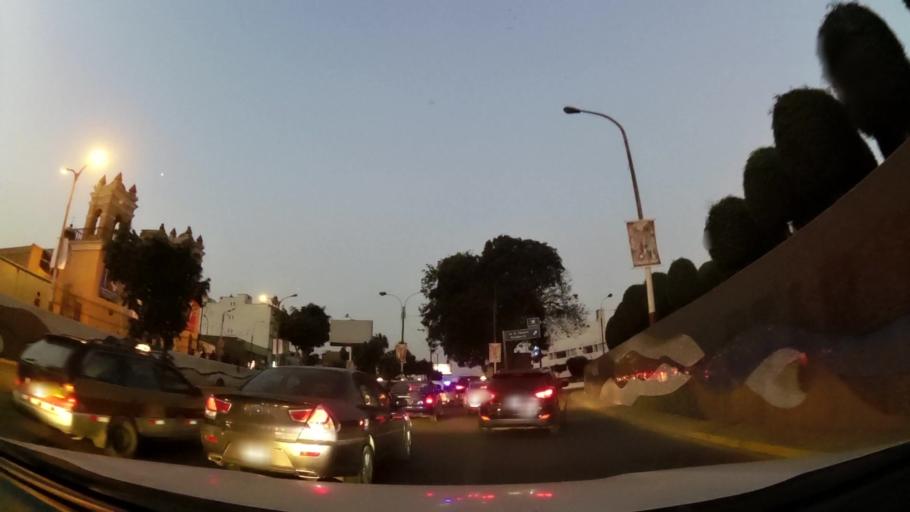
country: PE
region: Callao
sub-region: Callao
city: Callao
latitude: -12.0536
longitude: -77.0976
